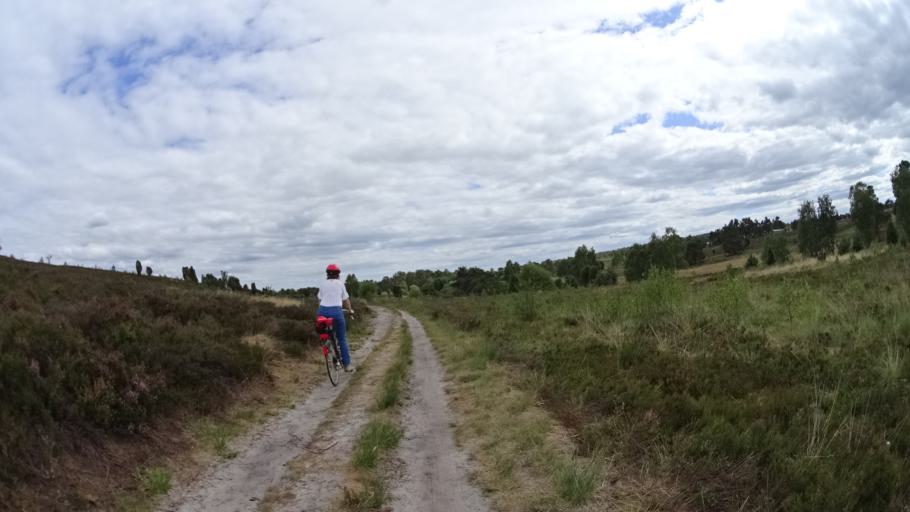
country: DE
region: Lower Saxony
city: Undeloh
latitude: 53.1854
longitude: 9.9941
